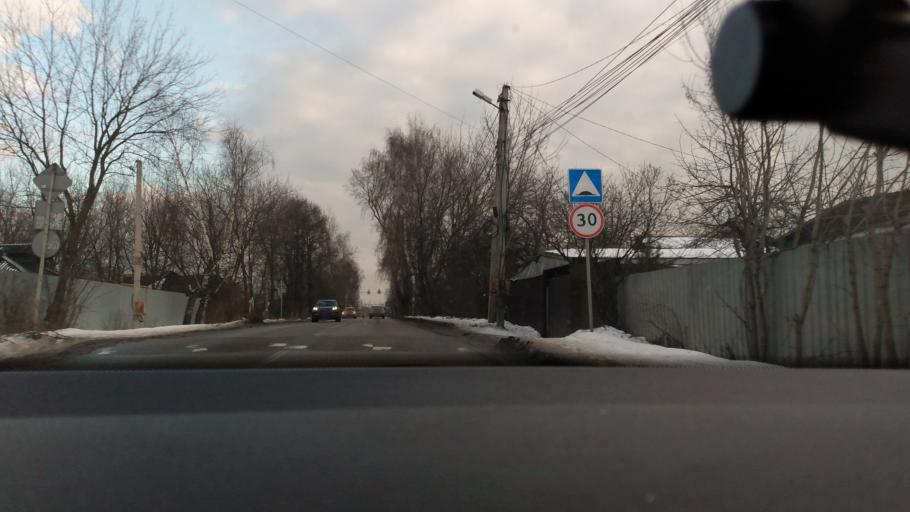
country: RU
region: Moskovskaya
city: Chornaya
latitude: 55.7071
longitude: 38.0486
